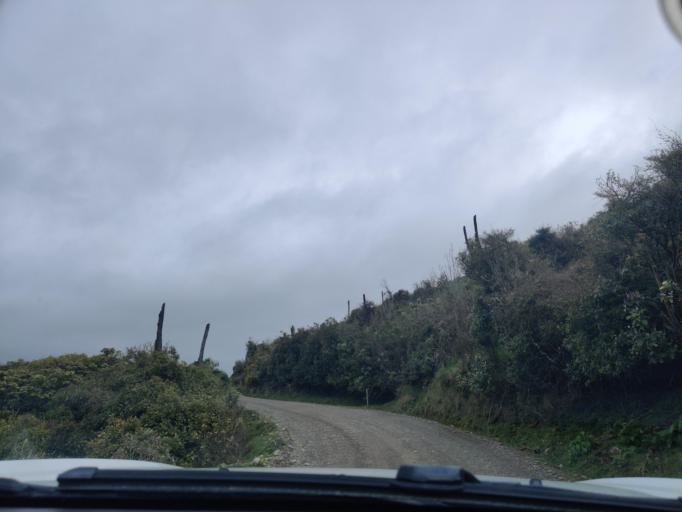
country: NZ
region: Manawatu-Wanganui
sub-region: Palmerston North City
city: Palmerston North
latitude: -40.2773
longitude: 175.8549
